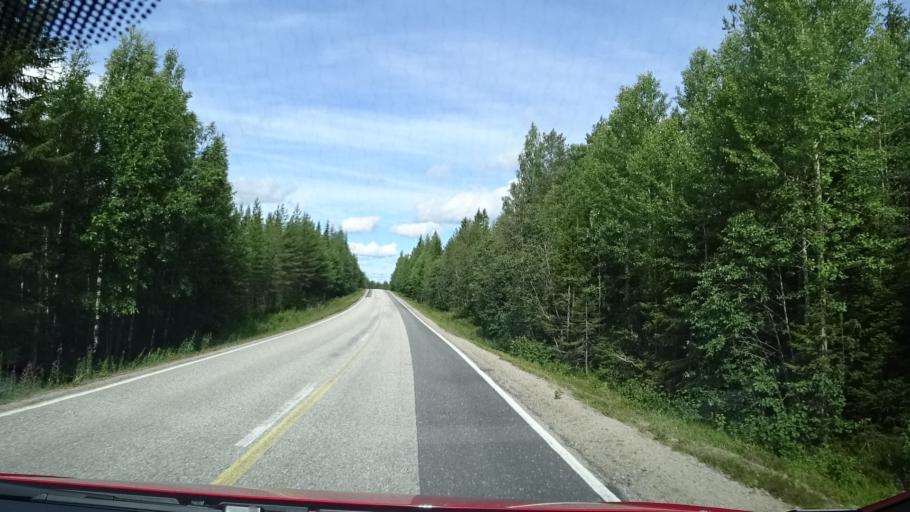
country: FI
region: Kainuu
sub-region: Kehys-Kainuu
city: Kuhmo
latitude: 64.4412
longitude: 29.8034
